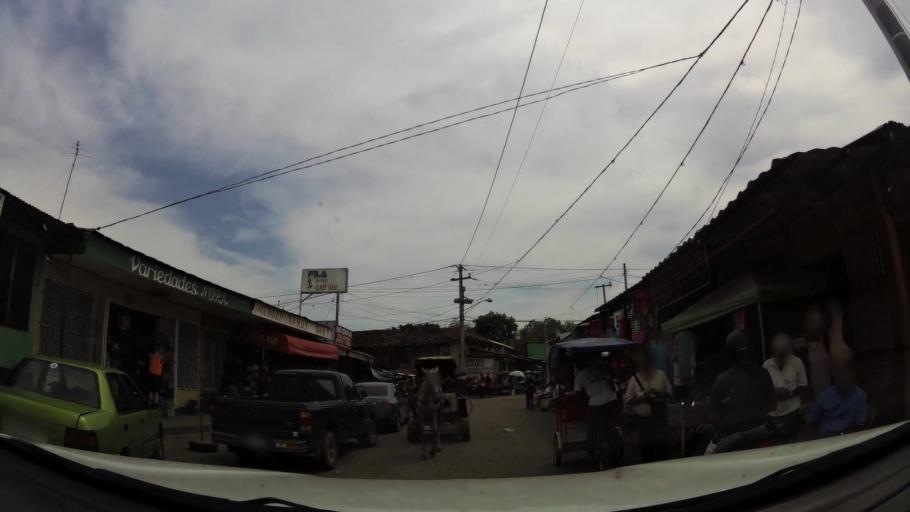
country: NI
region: Rivas
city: Rivas
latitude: 11.4405
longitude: -85.8319
